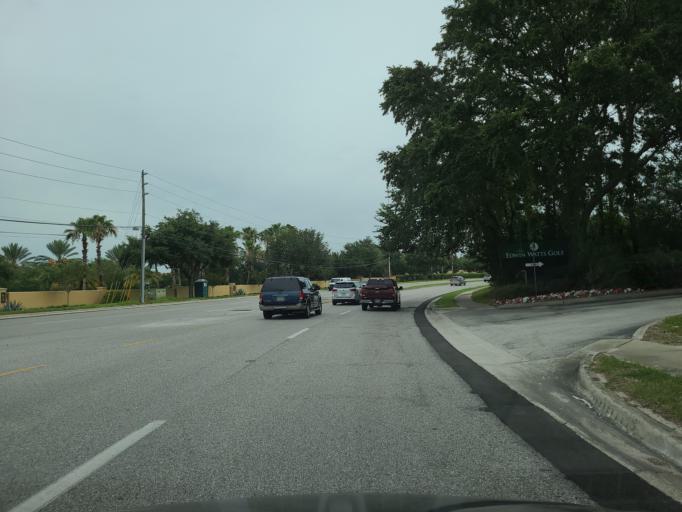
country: US
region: Florida
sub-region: Orange County
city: Doctor Phillips
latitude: 28.4551
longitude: -81.4775
